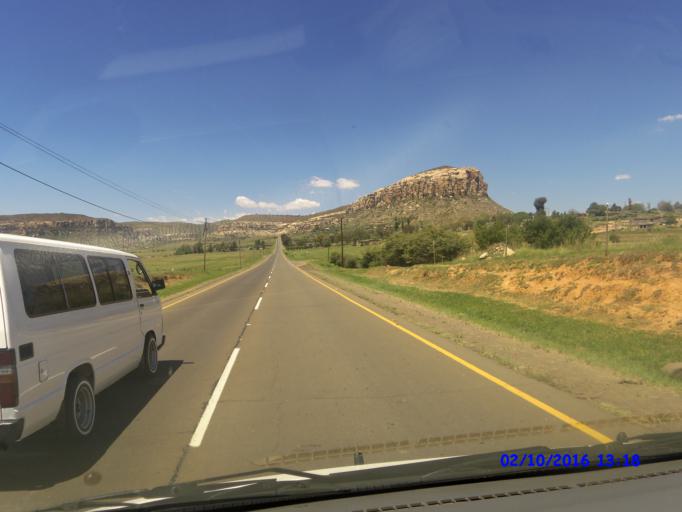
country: LS
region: Maseru
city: Nako
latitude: -29.4236
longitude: 27.6773
